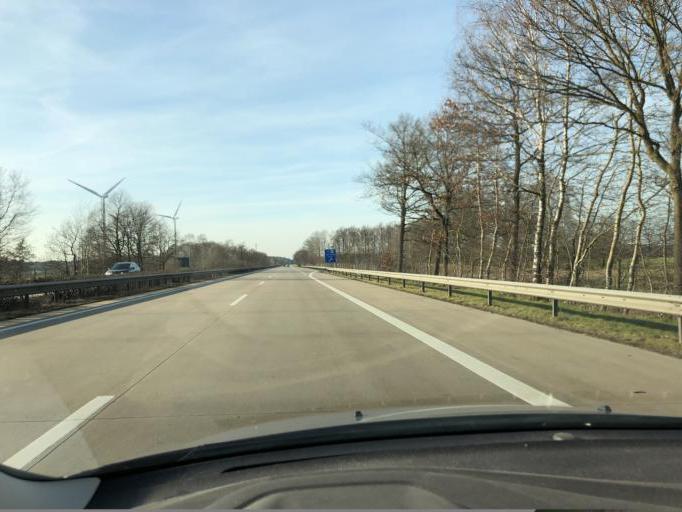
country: DE
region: Lower Saxony
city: Bohme
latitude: 52.8804
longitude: 9.4811
